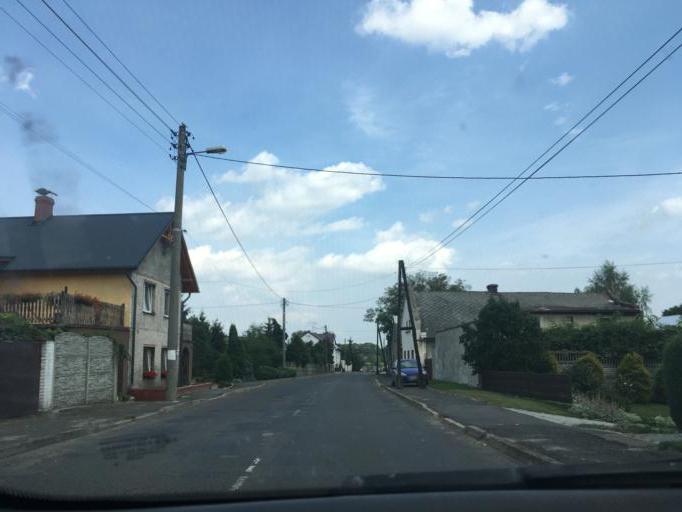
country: PL
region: Opole Voivodeship
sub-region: Powiat glubczycki
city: Baborow
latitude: 50.1213
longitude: 17.9295
